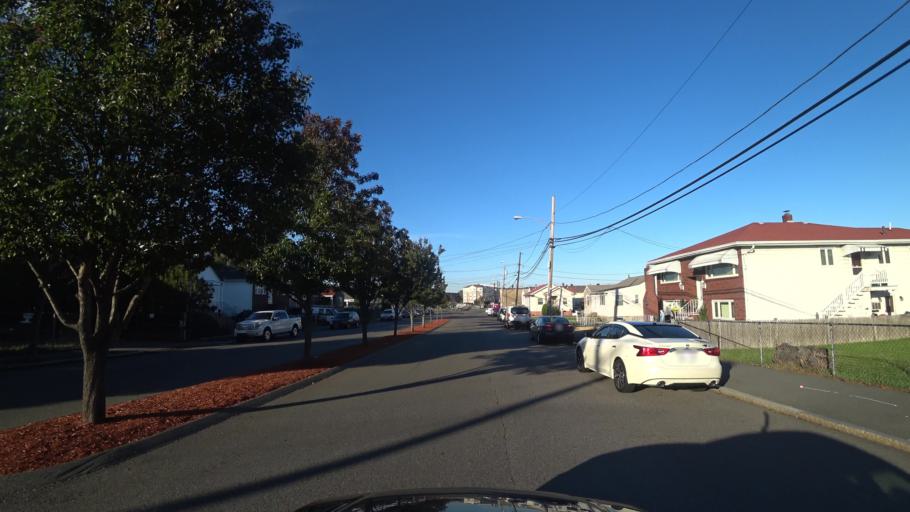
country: US
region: Massachusetts
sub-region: Suffolk County
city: Revere
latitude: 42.4217
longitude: -71.0094
